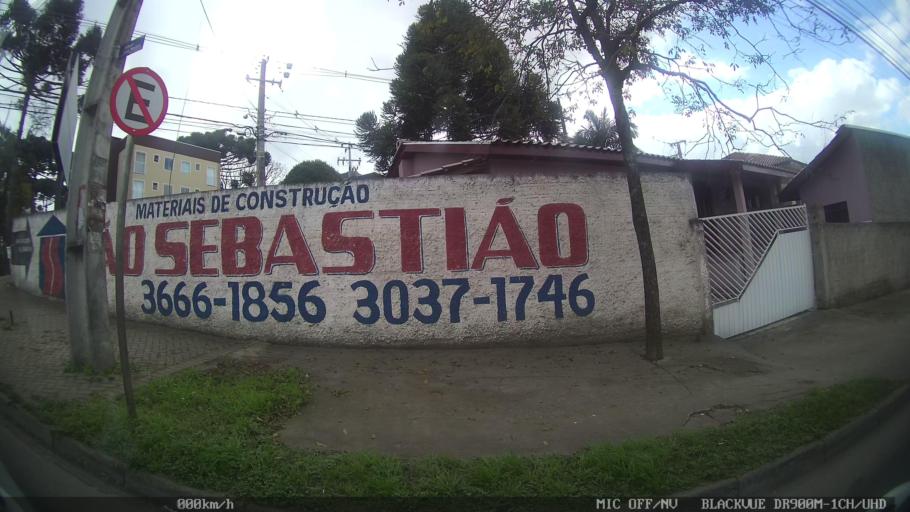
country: BR
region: Parana
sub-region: Colombo
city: Colombo
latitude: -25.3461
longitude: -49.1987
